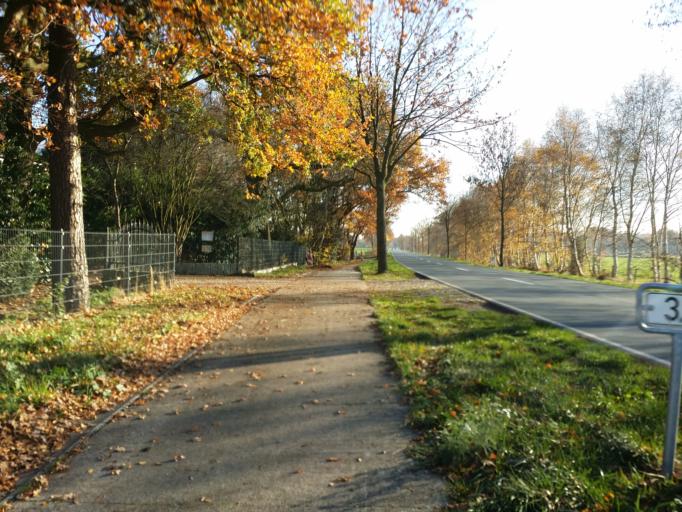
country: DE
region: Lower Saxony
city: Ottersberg
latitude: 53.0549
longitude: 9.1347
